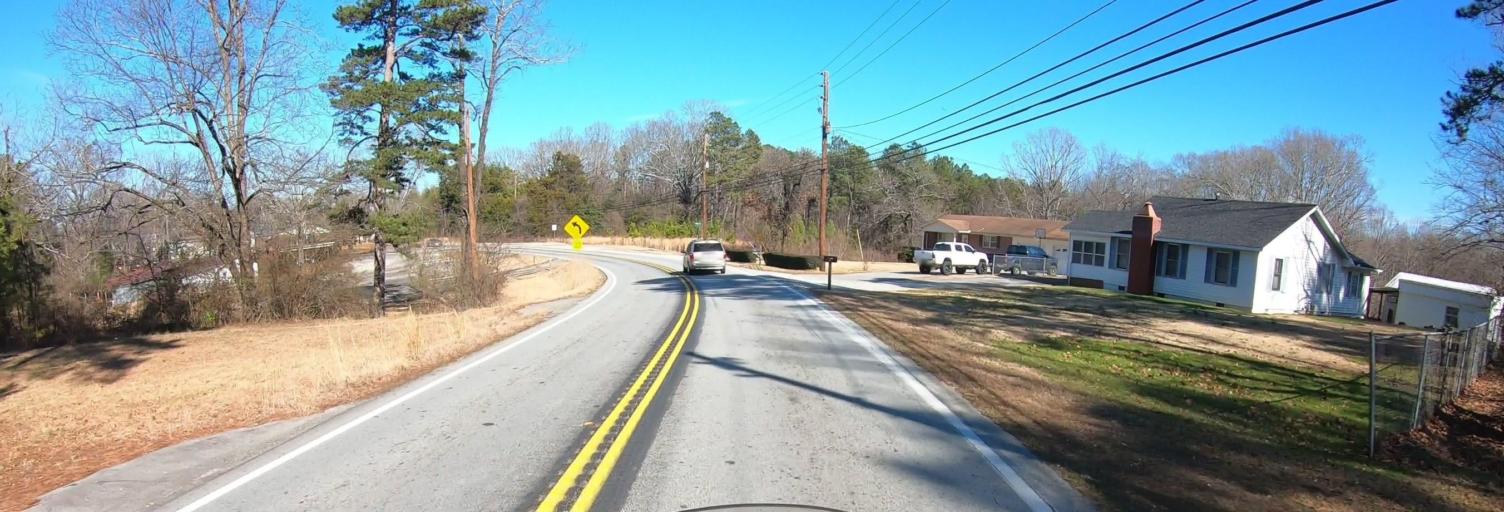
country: US
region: Georgia
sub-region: Stephens County
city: Toccoa
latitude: 34.5662
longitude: -83.3467
